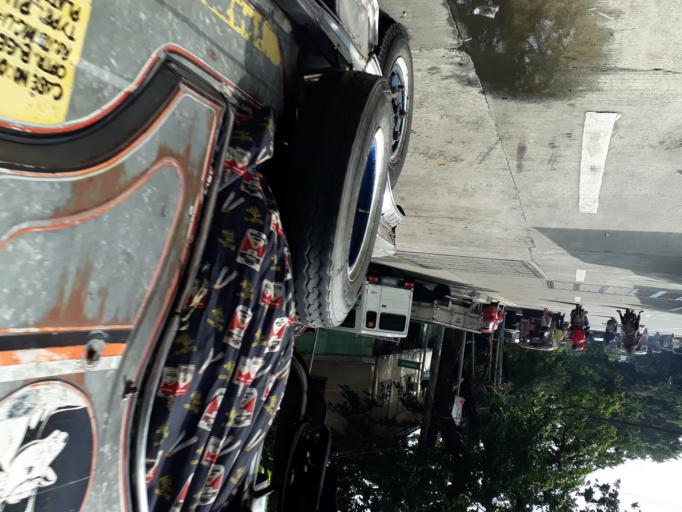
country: PH
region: Metro Manila
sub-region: City of Manila
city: Manila
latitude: 14.6278
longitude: 120.9845
